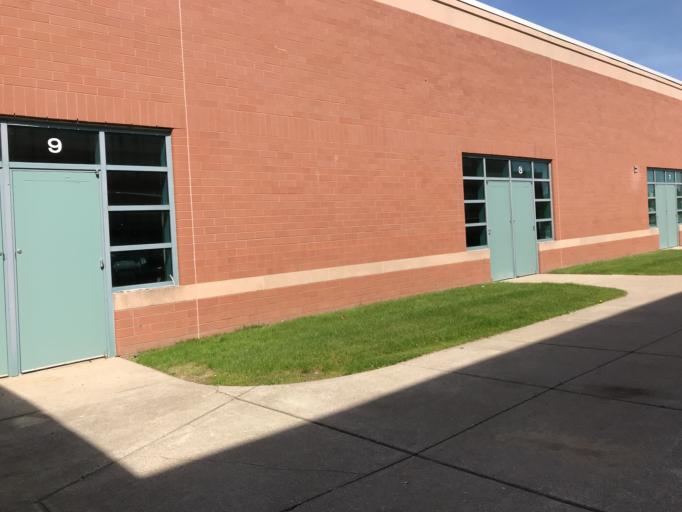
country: US
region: Michigan
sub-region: Oakland County
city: South Lyon
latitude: 42.4738
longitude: -83.6496
